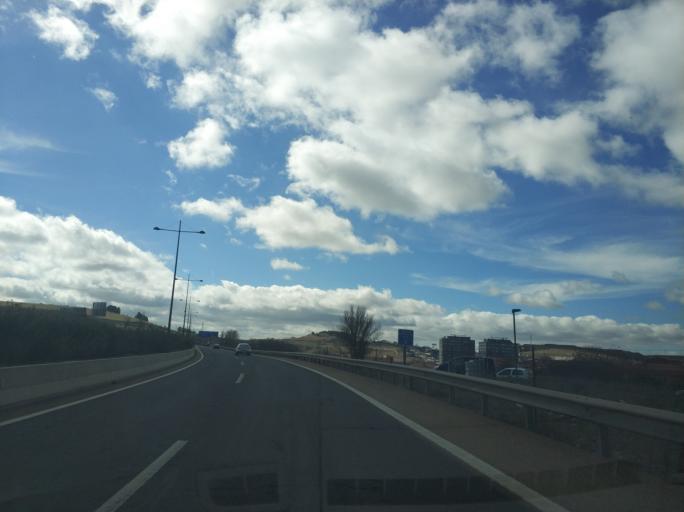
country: ES
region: Castille and Leon
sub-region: Provincia de Burgos
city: Burgos
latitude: 42.3317
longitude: -3.6969
